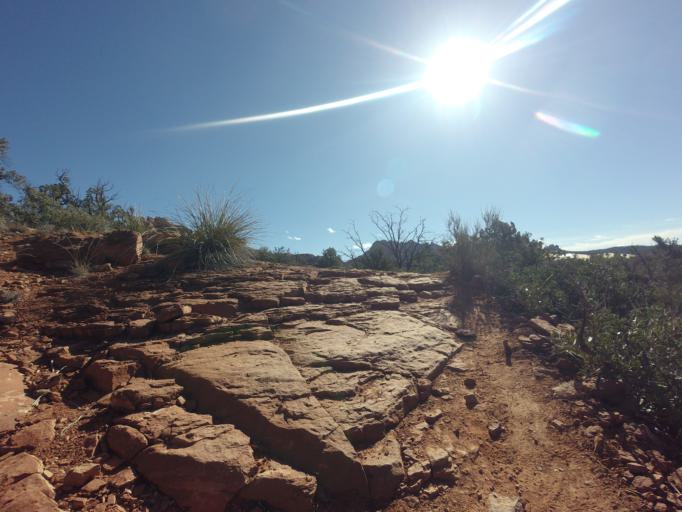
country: US
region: Arizona
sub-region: Yavapai County
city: Village of Oak Creek (Big Park)
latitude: 34.8139
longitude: -111.8038
